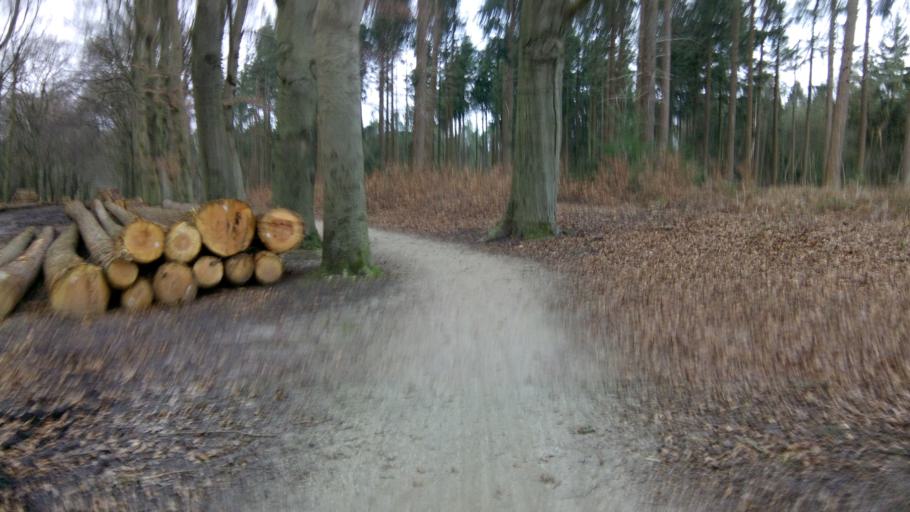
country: NL
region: Utrecht
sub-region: Gemeente Soest
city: Soest
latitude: 52.1791
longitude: 5.2370
